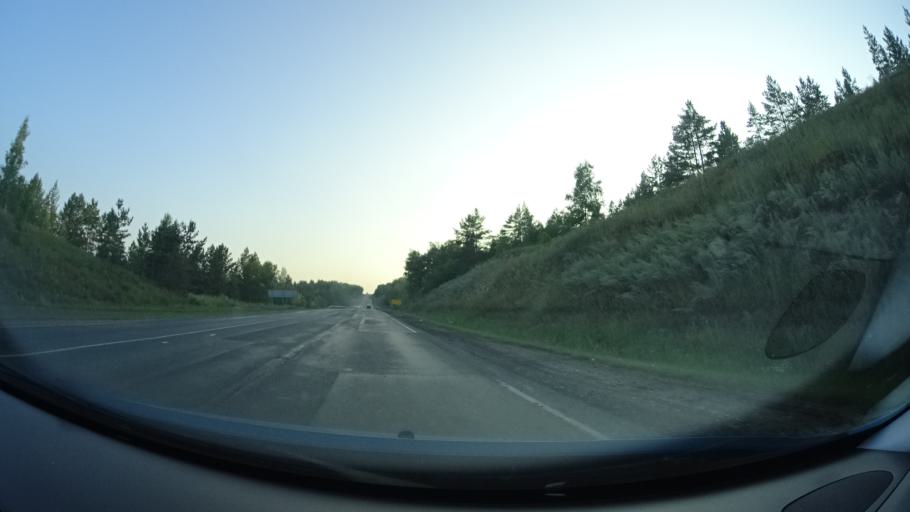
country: RU
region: Samara
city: Isakly
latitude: 53.9969
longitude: 51.5443
